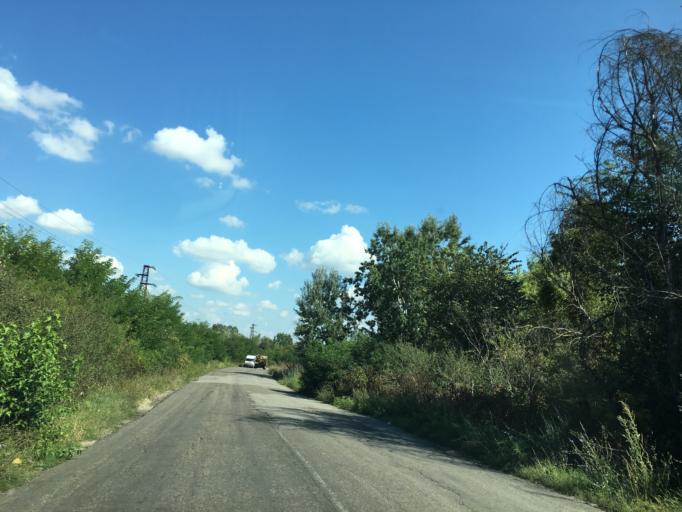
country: RO
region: Dolj
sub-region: Comuna Desa
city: Desa
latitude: 43.7723
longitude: 23.0759
